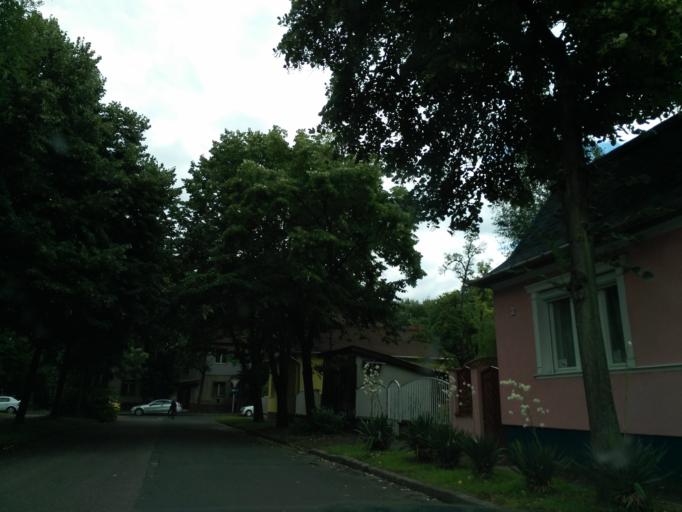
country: HU
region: Hajdu-Bihar
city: Debrecen
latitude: 47.5461
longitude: 21.6200
